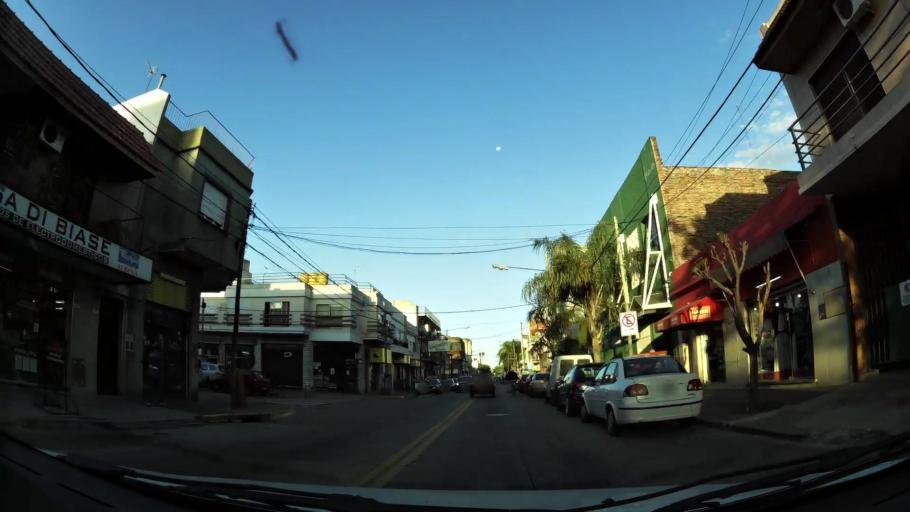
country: AR
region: Buenos Aires
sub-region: Partido de General San Martin
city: General San Martin
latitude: -34.5514
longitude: -58.5118
